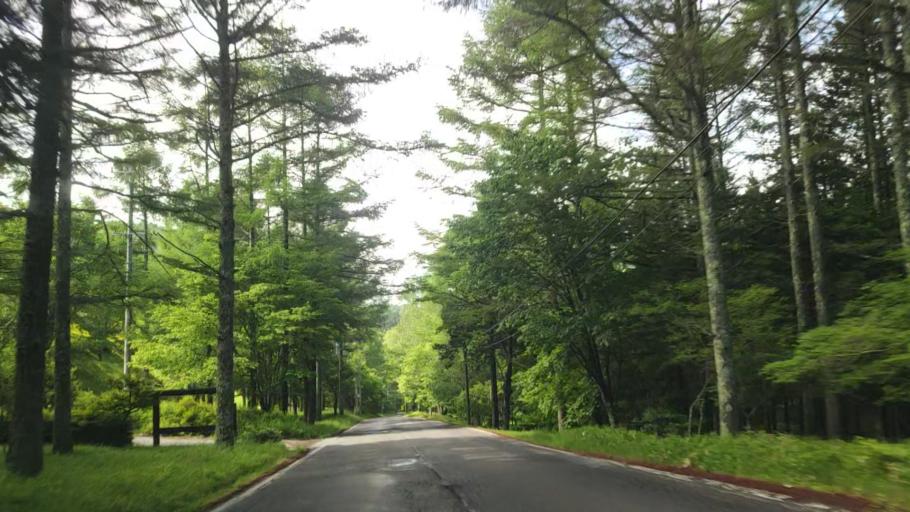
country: JP
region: Nagano
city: Suwa
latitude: 36.0881
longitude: 138.1437
